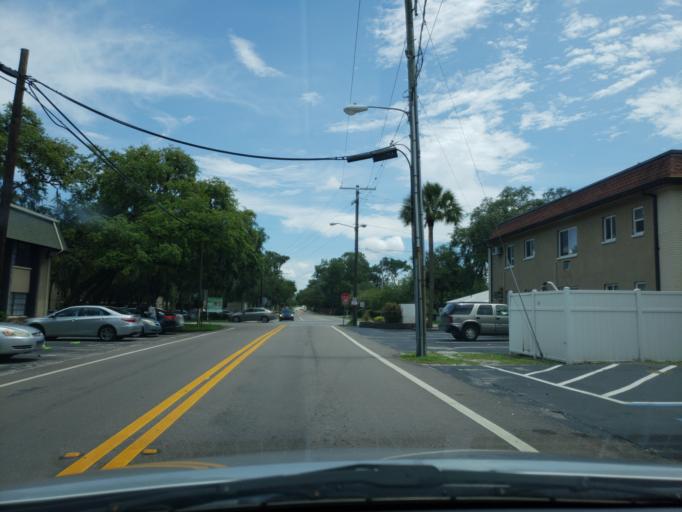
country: US
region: Florida
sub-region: Hillsborough County
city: University
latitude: 28.0807
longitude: -82.4142
